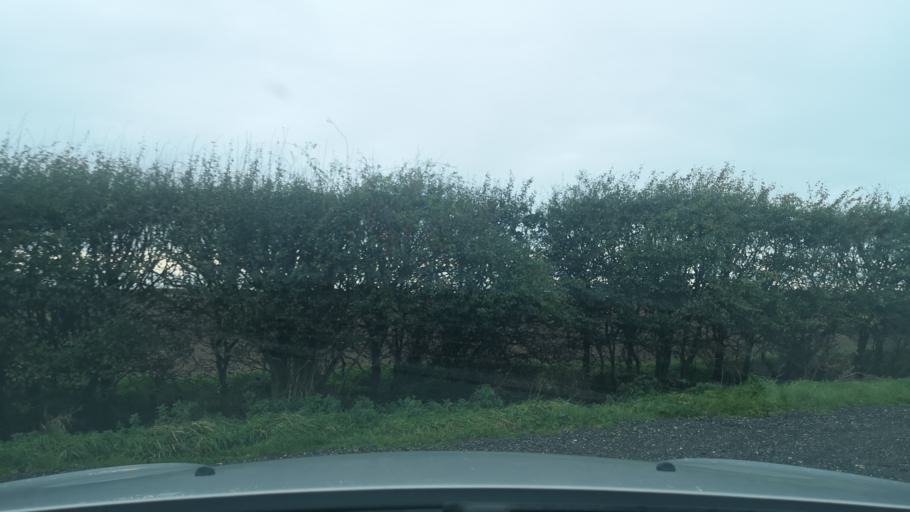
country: GB
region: England
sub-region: East Riding of Yorkshire
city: Easington
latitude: 53.6644
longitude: 0.0900
